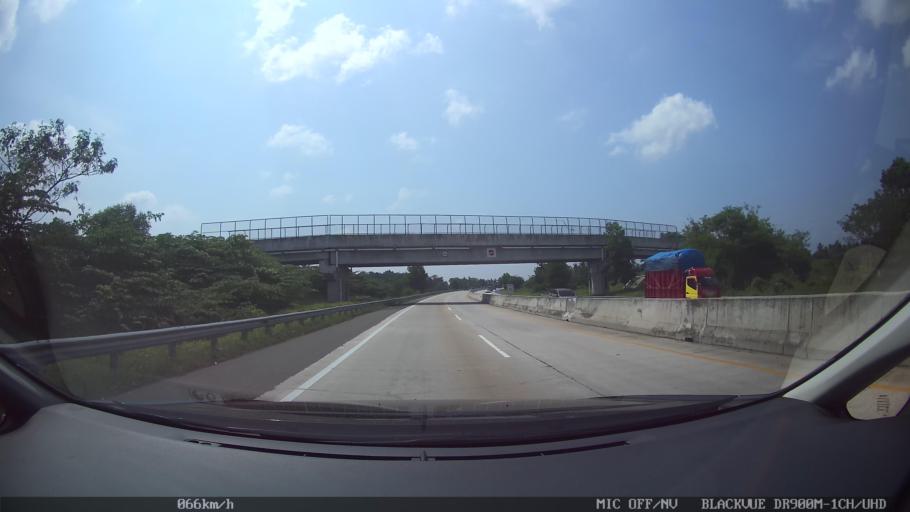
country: ID
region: Lampung
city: Natar
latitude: -5.2936
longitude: 105.2359
